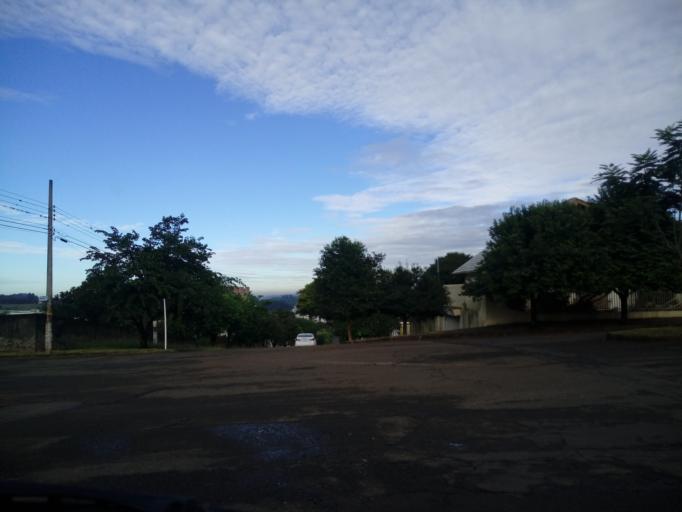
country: BR
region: Santa Catarina
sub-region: Chapeco
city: Chapeco
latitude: -27.1066
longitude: -52.6230
